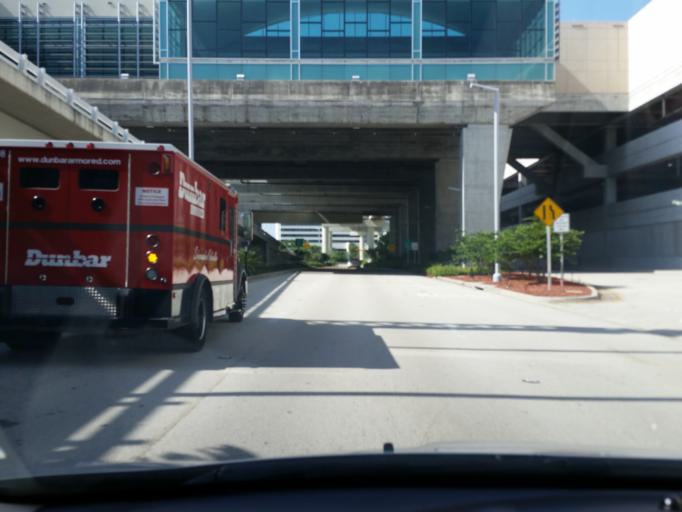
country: US
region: Florida
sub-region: Miami-Dade County
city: Brownsville
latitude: 25.7977
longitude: -80.2592
